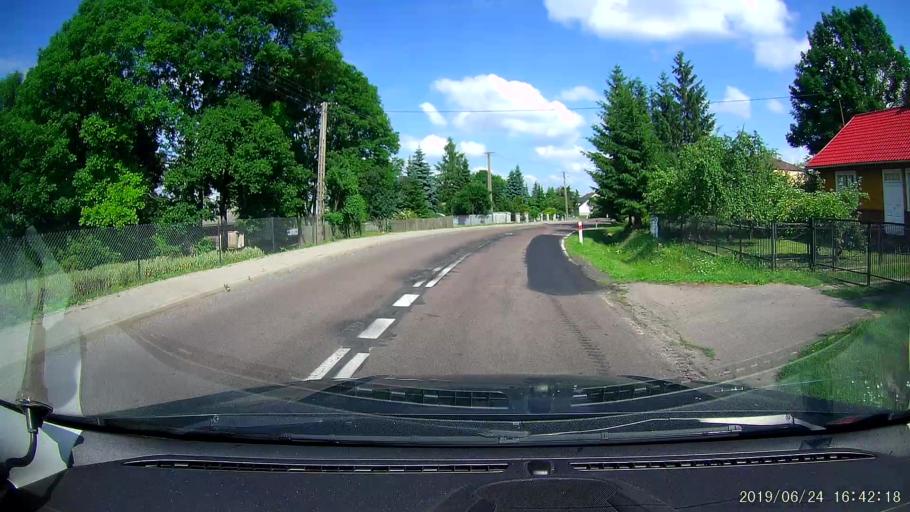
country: PL
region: Lublin Voivodeship
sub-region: Powiat tomaszowski
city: Michalow
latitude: 50.5354
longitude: 23.6138
